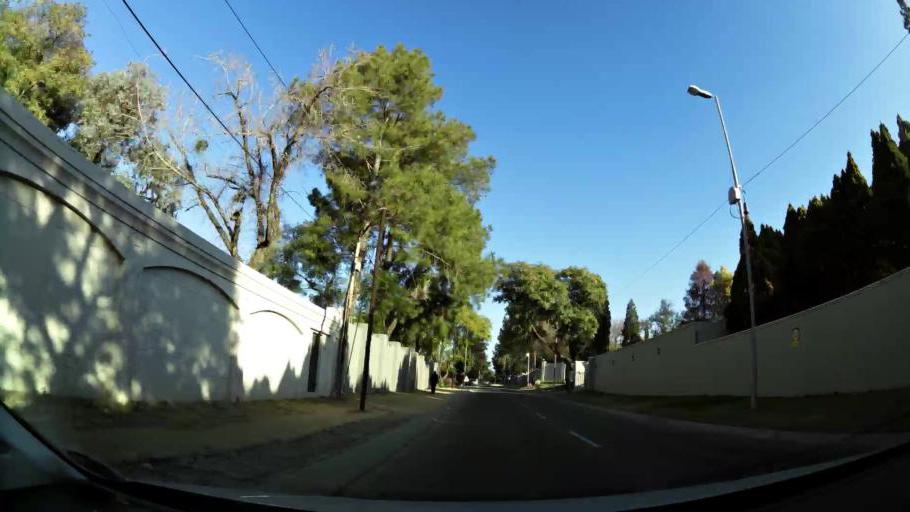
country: ZA
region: Gauteng
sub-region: City of Johannesburg Metropolitan Municipality
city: Modderfontein
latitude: -26.0866
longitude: 28.0694
